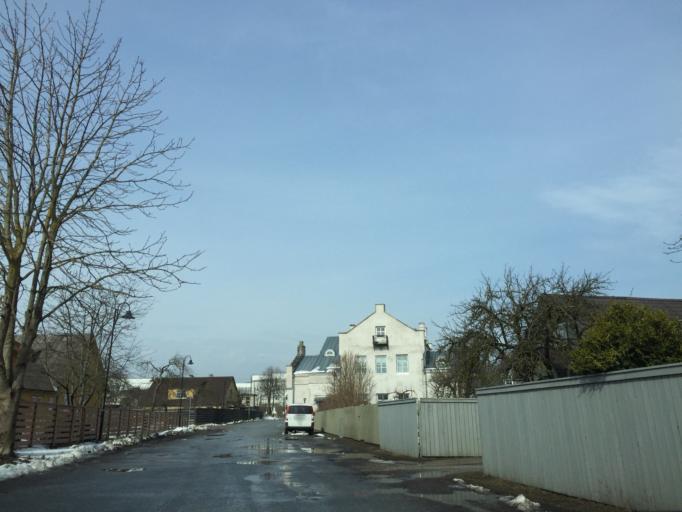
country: EE
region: Saare
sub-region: Kuressaare linn
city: Kuressaare
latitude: 58.2503
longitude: 22.4760
